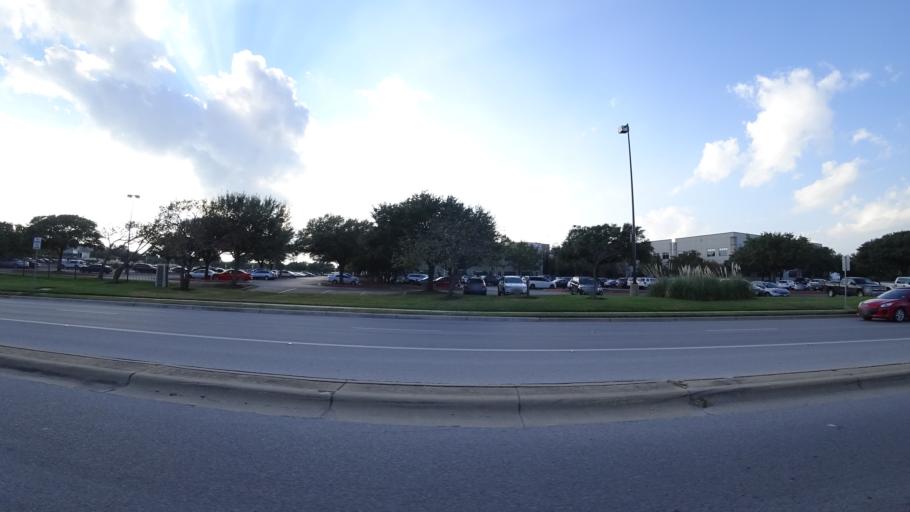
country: US
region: Texas
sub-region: Williamson County
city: Round Rock
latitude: 30.4865
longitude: -97.6620
